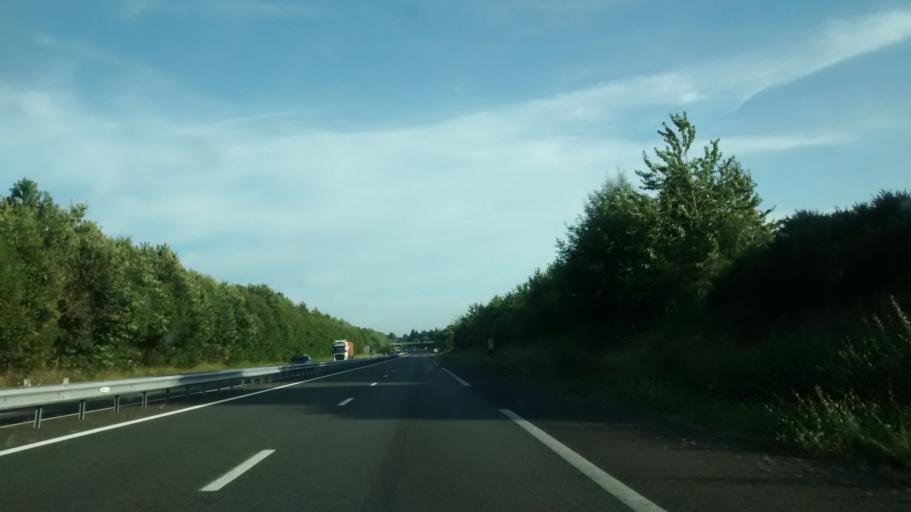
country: FR
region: Brittany
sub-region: Departement d'Ille-et-Vilaine
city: Saint-Etienne-en-Cogles
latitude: 48.4461
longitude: -1.3249
